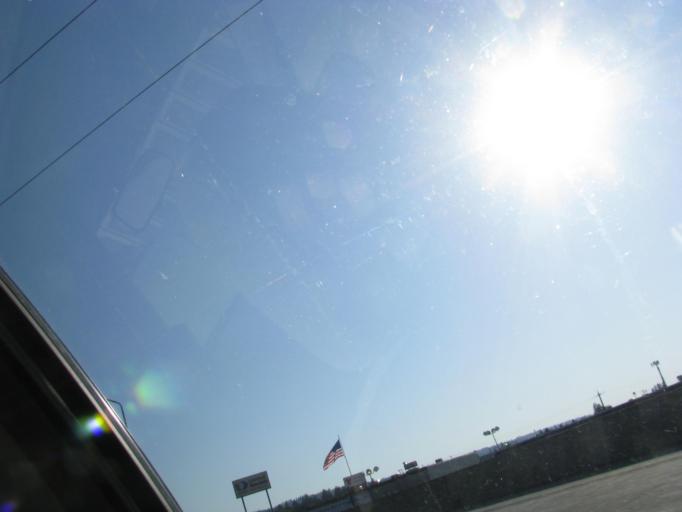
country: US
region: Washington
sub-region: Spokane County
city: Dishman
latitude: 47.6556
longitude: -117.3252
